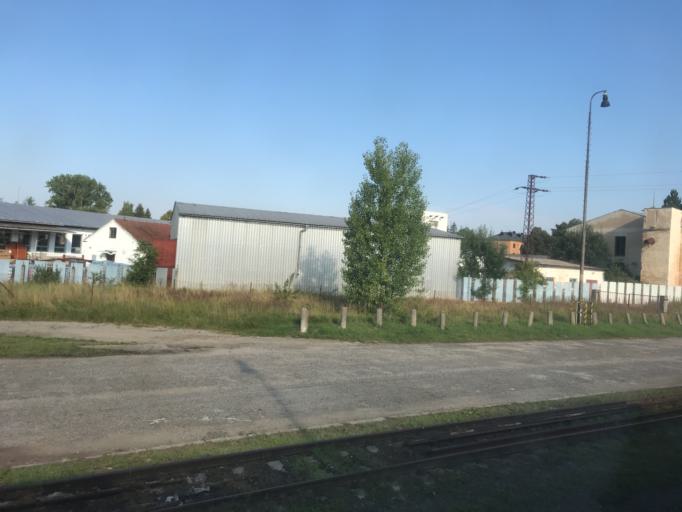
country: CZ
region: Jihocesky
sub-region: Okres Jindrichuv Hradec
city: Trebon
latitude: 49.0134
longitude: 14.7617
